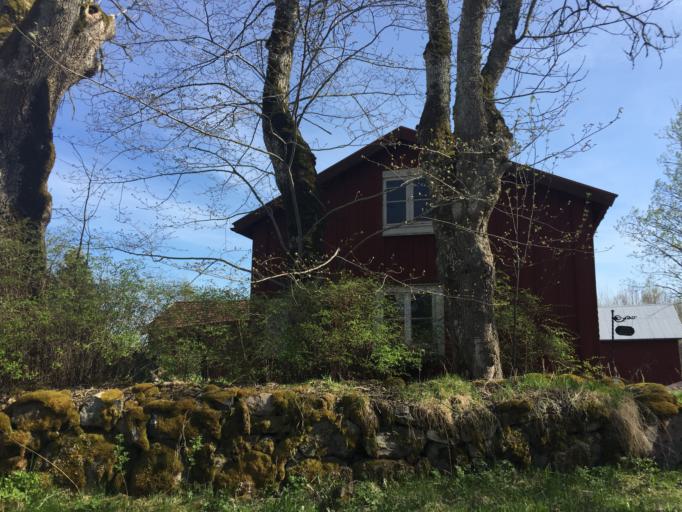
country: SE
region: OErebro
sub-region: Lekebergs Kommun
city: Fjugesta
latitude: 59.1800
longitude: 14.9284
